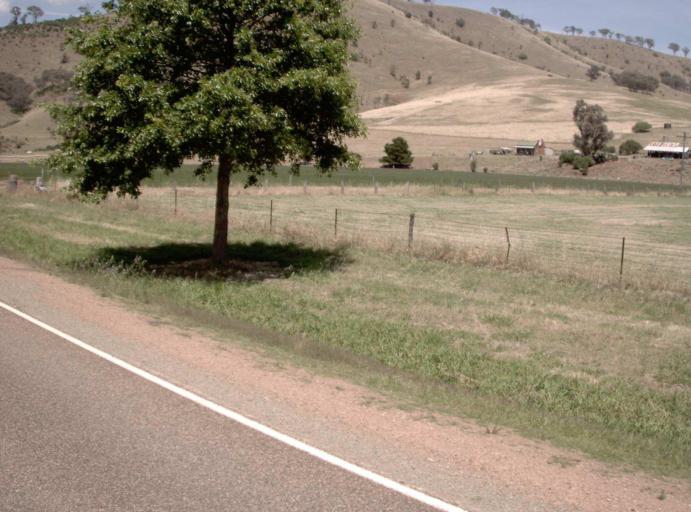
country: AU
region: Victoria
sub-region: East Gippsland
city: Bairnsdale
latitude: -37.2541
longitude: 147.7115
